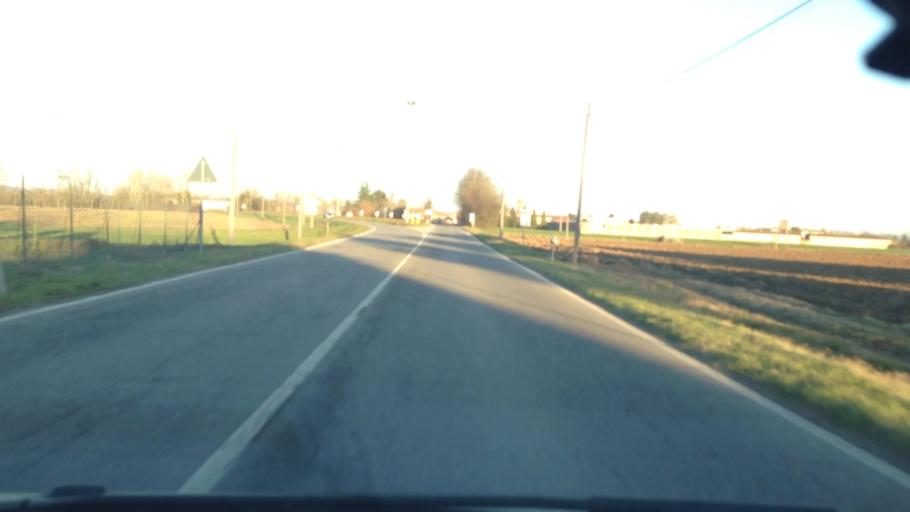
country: IT
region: Piedmont
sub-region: Provincia di Alessandria
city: Solero
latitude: 44.9168
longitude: 8.4948
